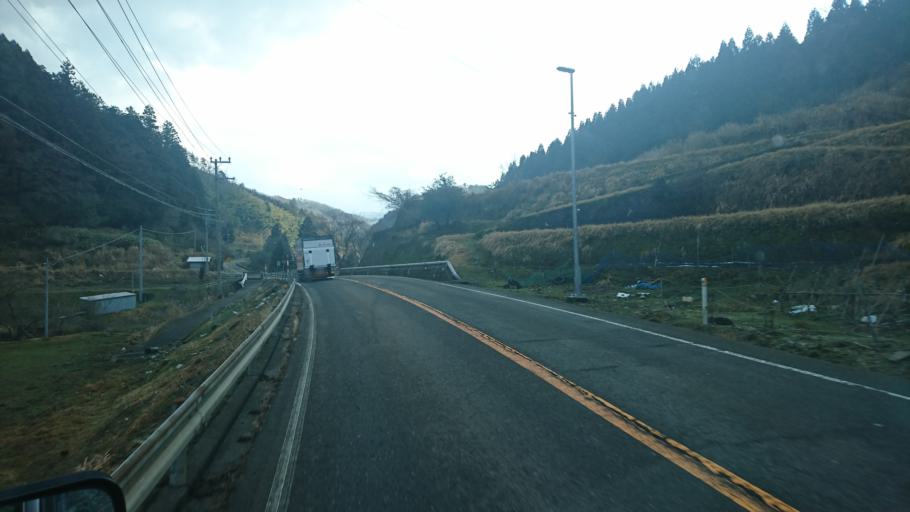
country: JP
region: Tottori
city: Tottori
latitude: 35.5405
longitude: 134.5080
